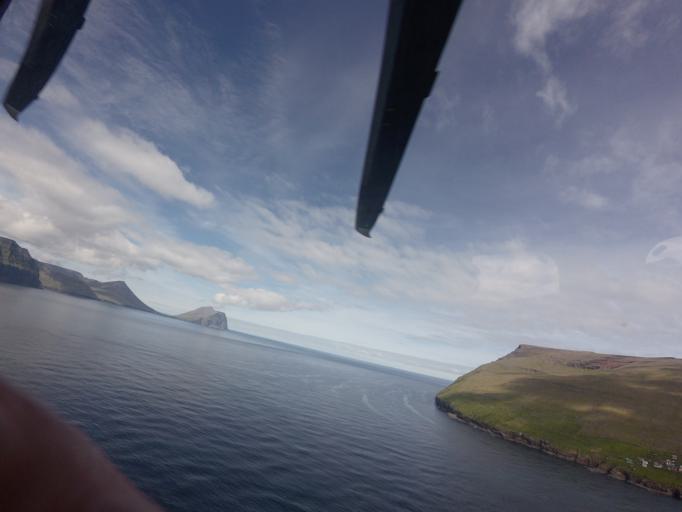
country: FO
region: Nordoyar
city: Klaksvik
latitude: 62.3084
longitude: -6.3228
